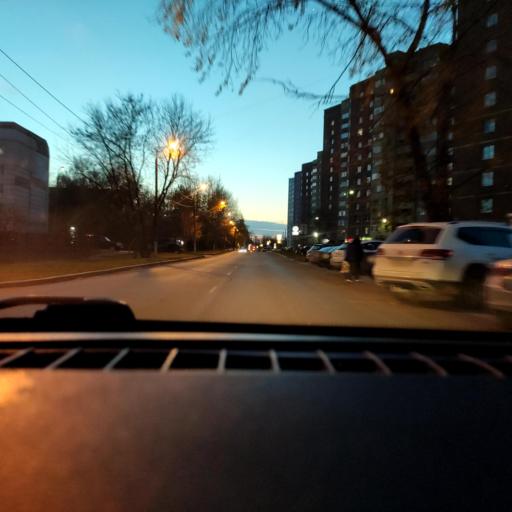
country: RU
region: Perm
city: Perm
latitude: 58.0636
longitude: 56.3552
